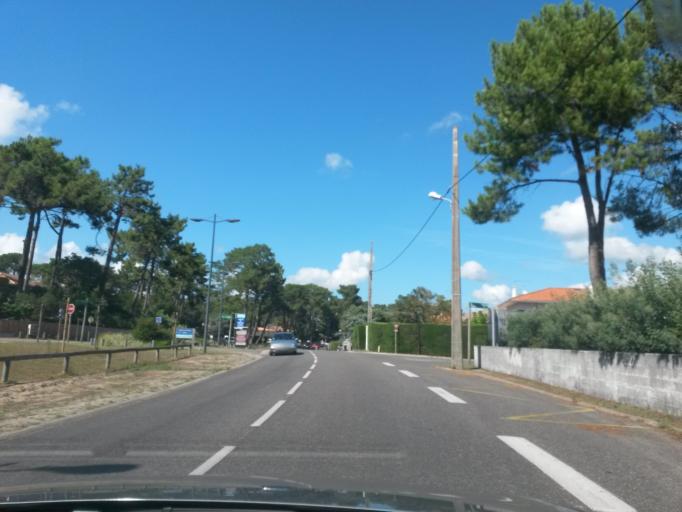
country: FR
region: Aquitaine
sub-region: Departement de la Gironde
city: Arcachon
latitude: 44.7069
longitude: -1.2246
